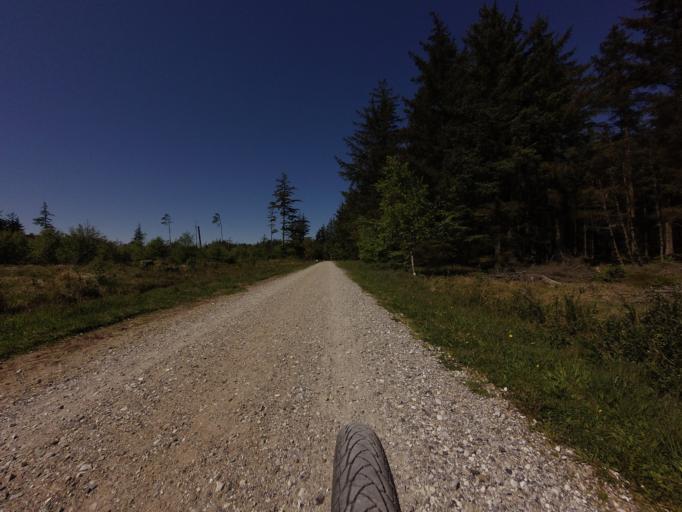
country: DK
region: North Denmark
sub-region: Jammerbugt Kommune
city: Pandrup
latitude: 57.2422
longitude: 9.5887
